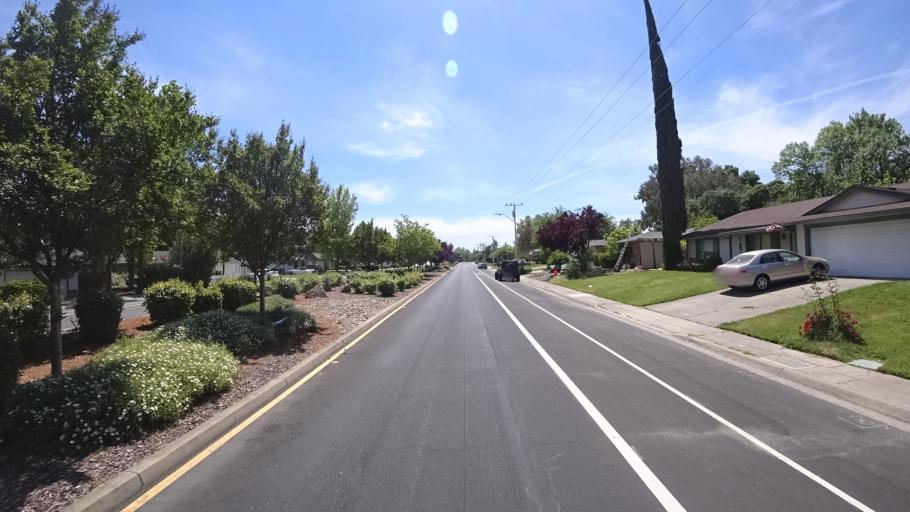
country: US
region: California
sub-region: Placer County
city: Rocklin
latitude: 38.7890
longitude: -121.2518
